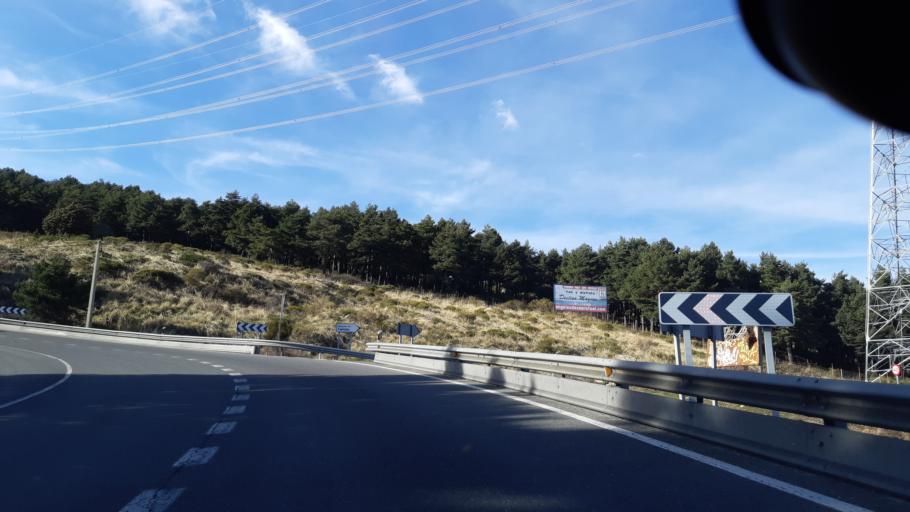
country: ES
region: Madrid
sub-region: Provincia de Madrid
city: Guadarrama
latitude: 40.7091
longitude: -4.1277
